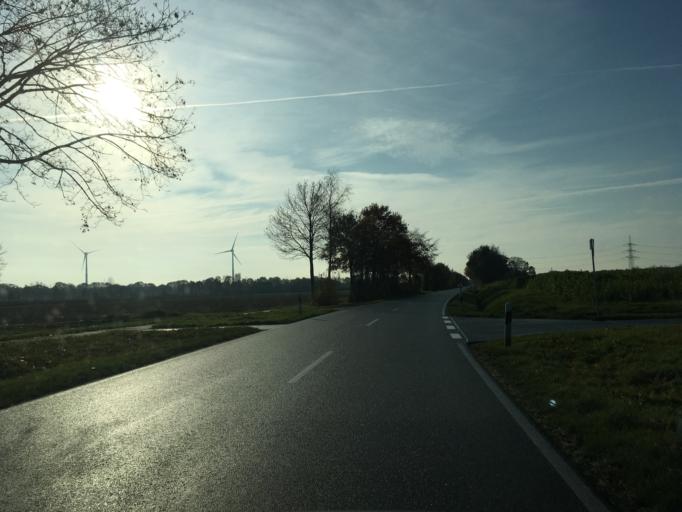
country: DE
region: North Rhine-Westphalia
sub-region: Regierungsbezirk Munster
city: Ahaus
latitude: 52.0431
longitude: 6.9706
